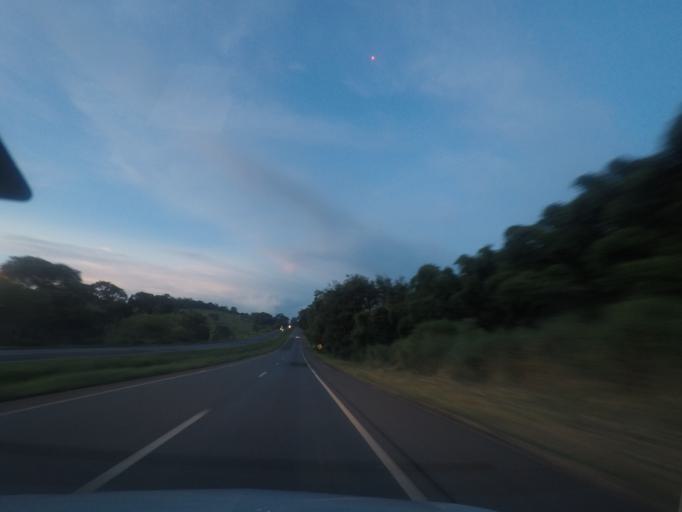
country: BR
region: Goias
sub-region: Pontalina
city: Pontalina
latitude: -17.4924
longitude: -49.2127
